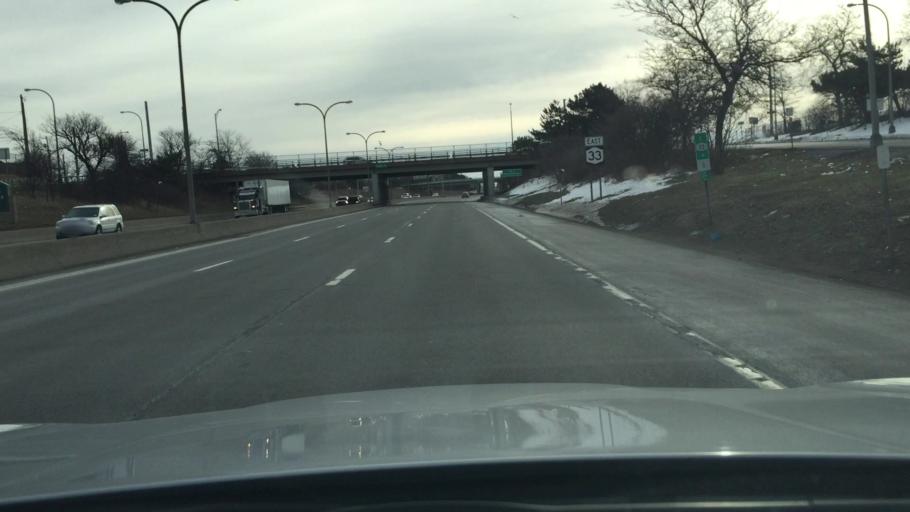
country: US
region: New York
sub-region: Erie County
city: Eggertsville
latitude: 42.9331
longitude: -78.8007
